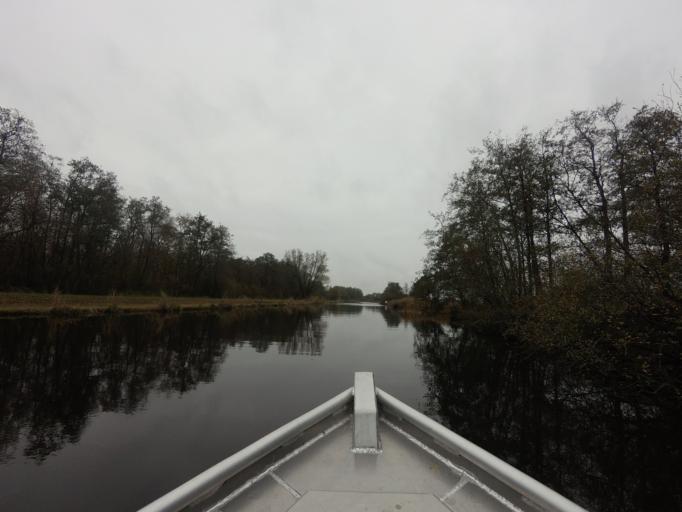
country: NL
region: Overijssel
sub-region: Gemeente Steenwijkerland
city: Oldemarkt
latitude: 52.7755
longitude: 5.9715
